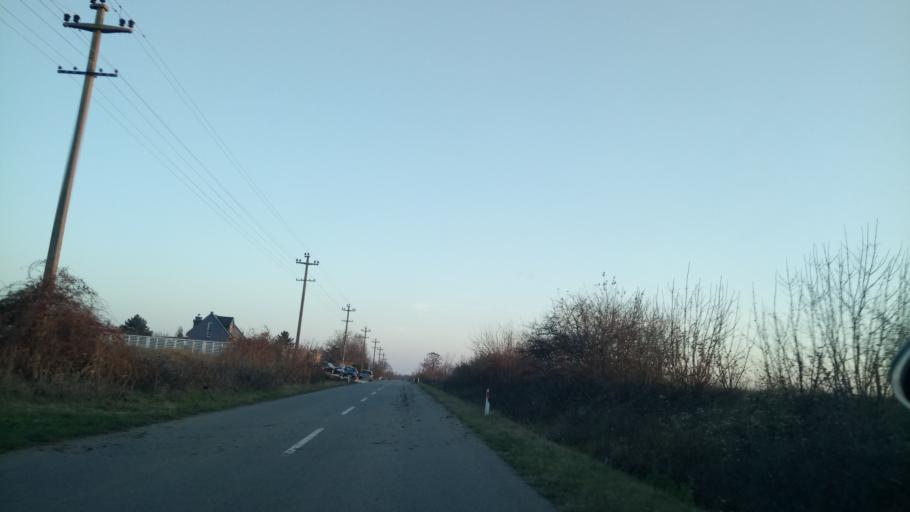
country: RS
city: Surduk
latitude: 45.0932
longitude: 20.2970
